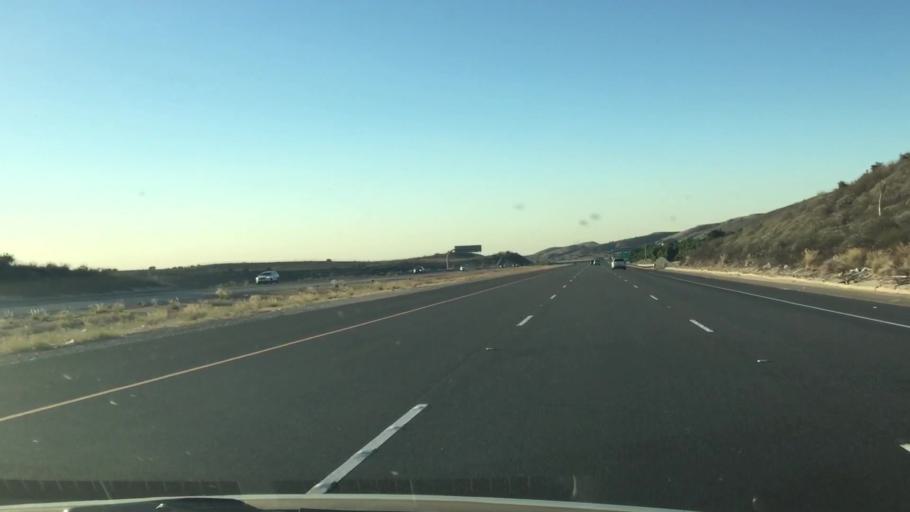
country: US
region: California
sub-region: Orange County
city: Foothill Ranch
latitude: 33.6873
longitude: -117.6802
